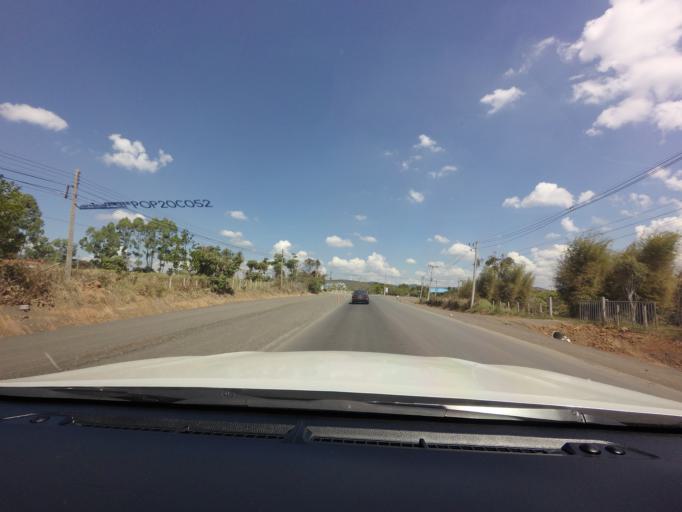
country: TH
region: Nakhon Ratchasima
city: Wang Nam Khiao
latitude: 14.3676
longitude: 101.8995
